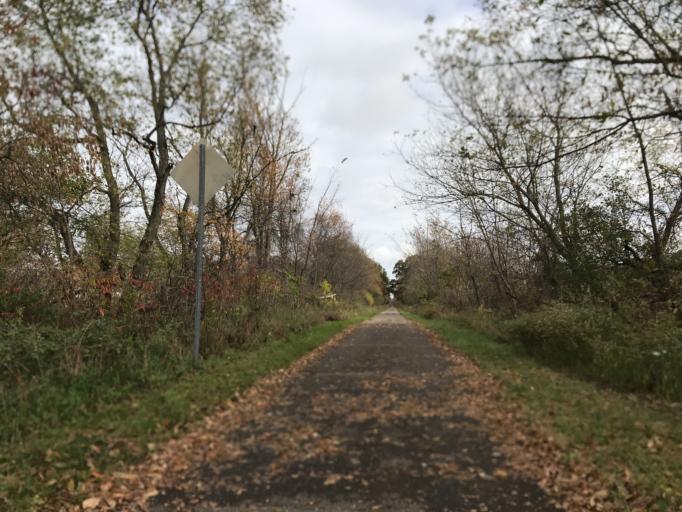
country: US
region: Michigan
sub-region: Oakland County
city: South Lyon
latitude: 42.4896
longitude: -83.6304
